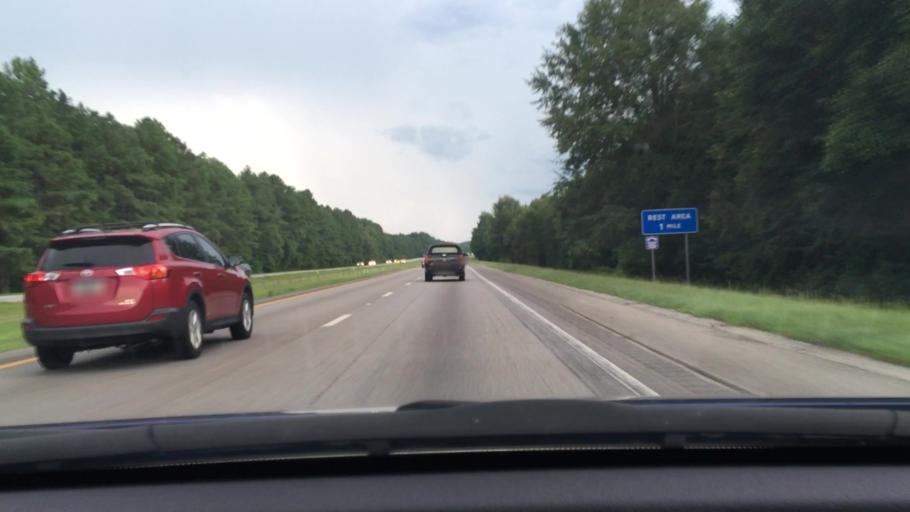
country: US
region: South Carolina
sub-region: Kershaw County
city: Lugoff
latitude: 34.2105
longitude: -80.6467
